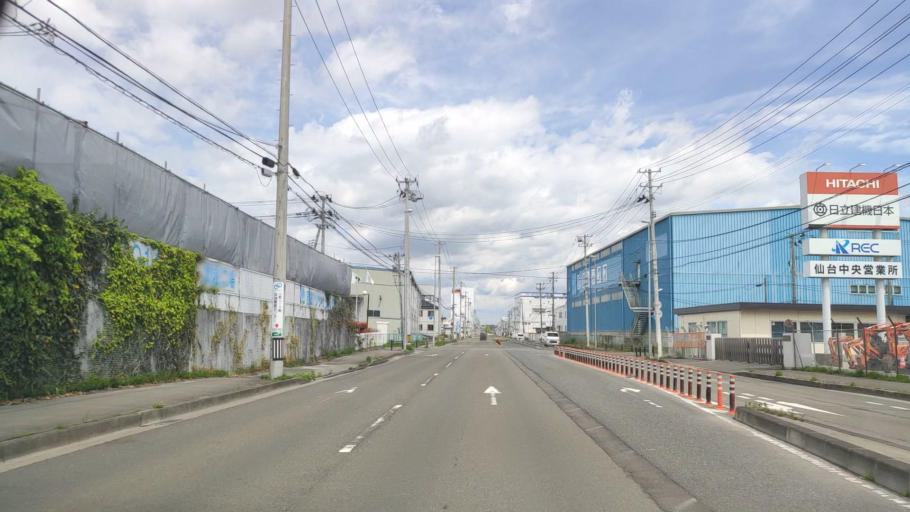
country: JP
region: Miyagi
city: Sendai-shi
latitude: 38.2621
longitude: 140.9430
